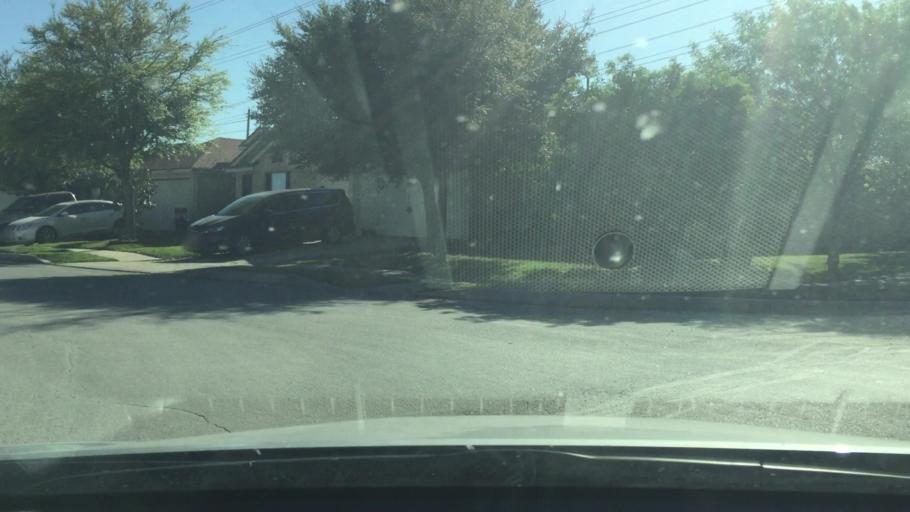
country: US
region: Texas
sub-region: Bexar County
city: Converse
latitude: 29.4678
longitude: -98.3229
